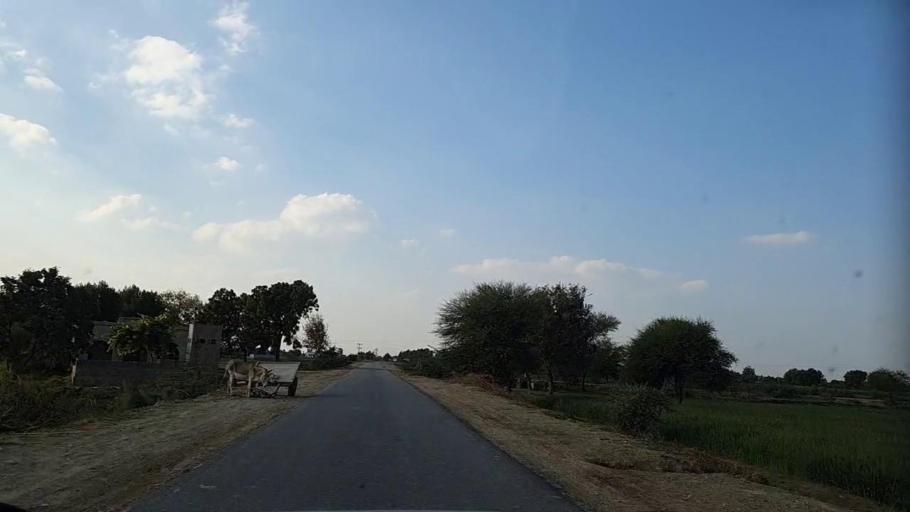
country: PK
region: Sindh
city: Pithoro
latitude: 25.6854
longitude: 69.2247
